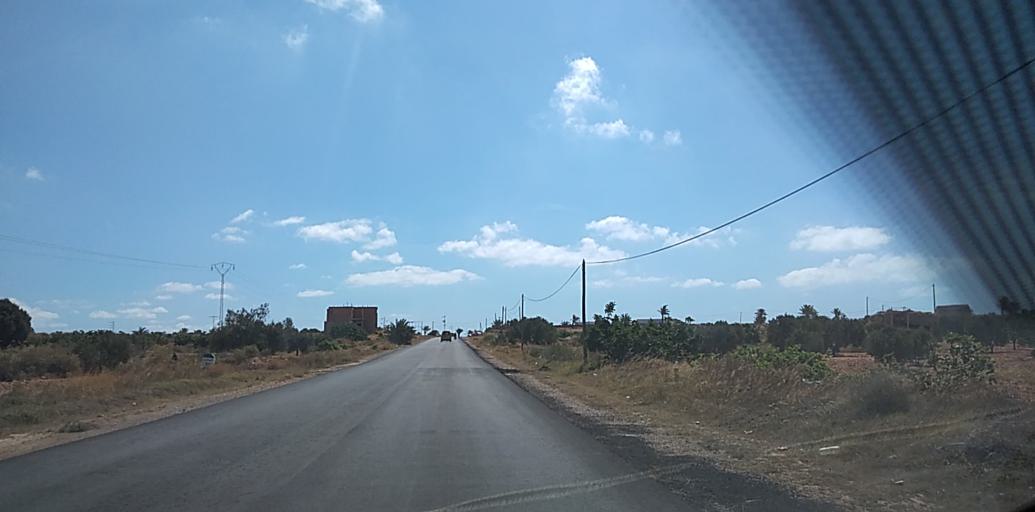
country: TN
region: Safaqis
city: Al Qarmadah
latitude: 34.6575
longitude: 11.0783
